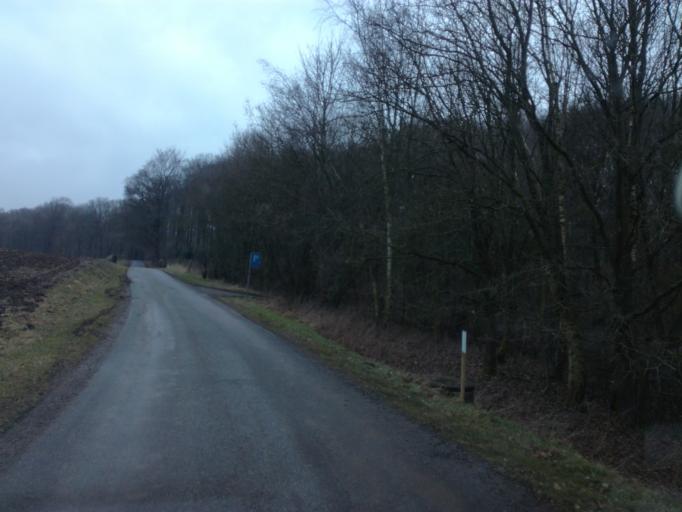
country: DK
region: South Denmark
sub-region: Vejle Kommune
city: Brejning
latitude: 55.6171
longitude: 9.7045
